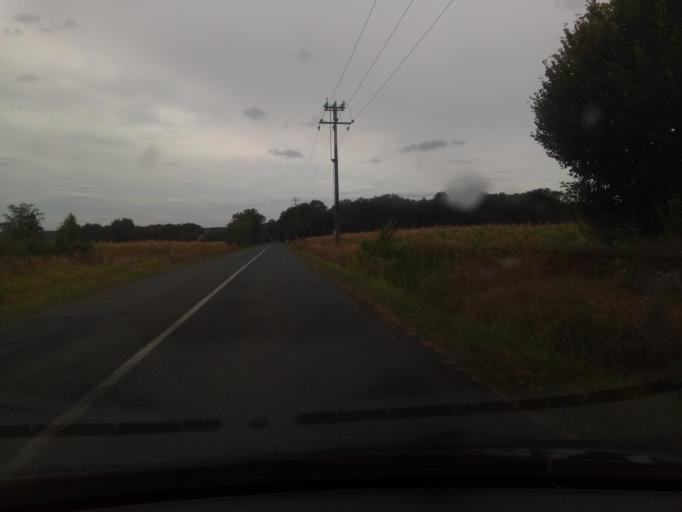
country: FR
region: Poitou-Charentes
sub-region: Departement de la Vienne
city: Pleumartin
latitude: 46.6813
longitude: 0.8571
